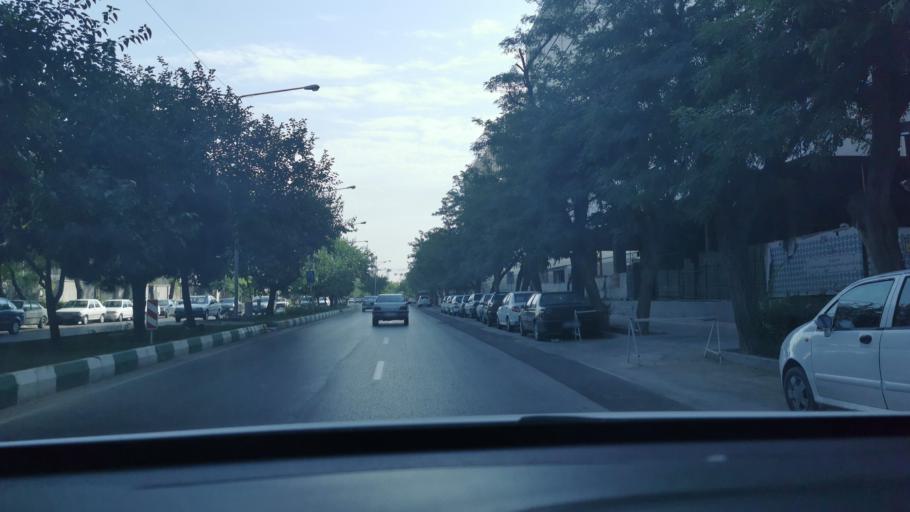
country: IR
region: Razavi Khorasan
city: Mashhad
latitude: 36.3175
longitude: 59.5600
